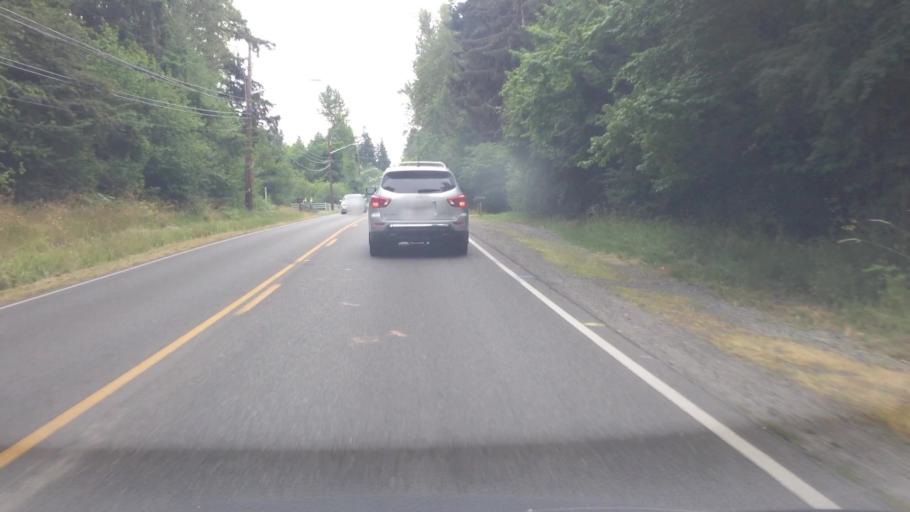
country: US
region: Washington
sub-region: Pierce County
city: South Hill
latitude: 47.1285
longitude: -122.3040
